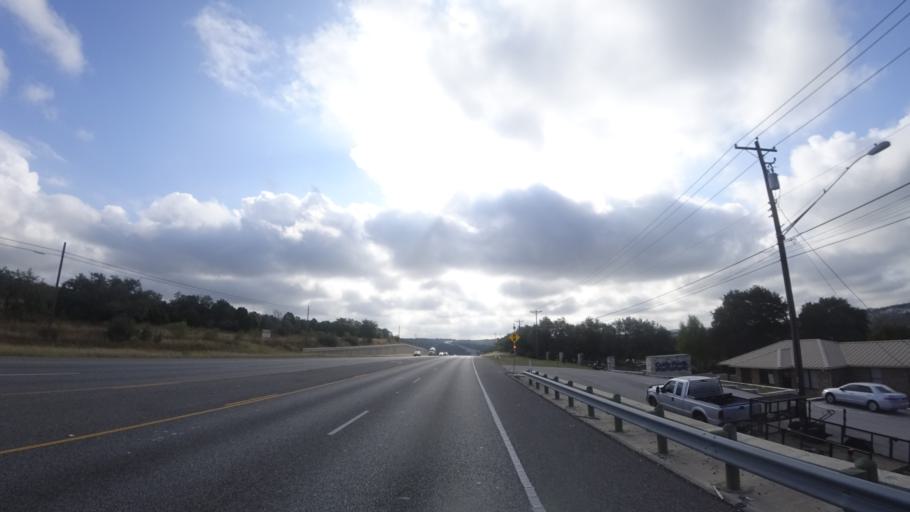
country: US
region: Texas
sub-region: Travis County
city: Bee Cave
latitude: 30.3010
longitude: -97.9304
